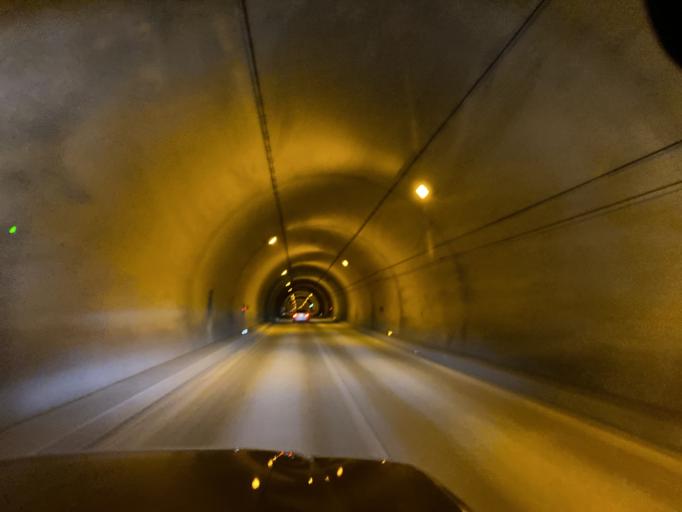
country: JP
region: Gifu
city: Takayama
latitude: 36.1245
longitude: 136.9090
